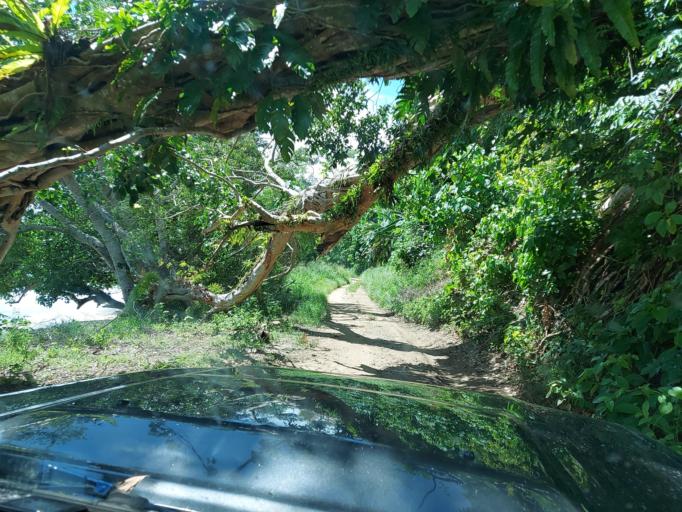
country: VU
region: Malampa
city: Lakatoro
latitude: -16.3288
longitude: 167.7291
